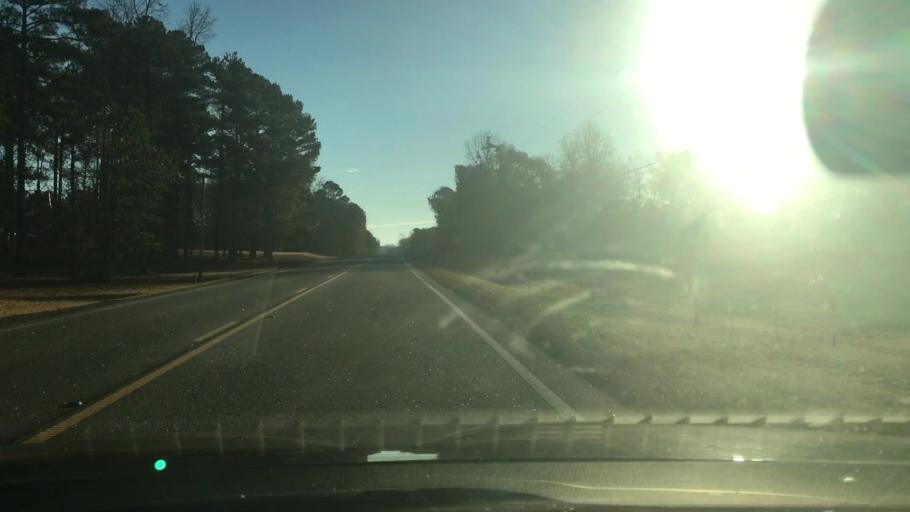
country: US
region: Georgia
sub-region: Coweta County
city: Senoia
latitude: 33.2530
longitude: -84.4828
